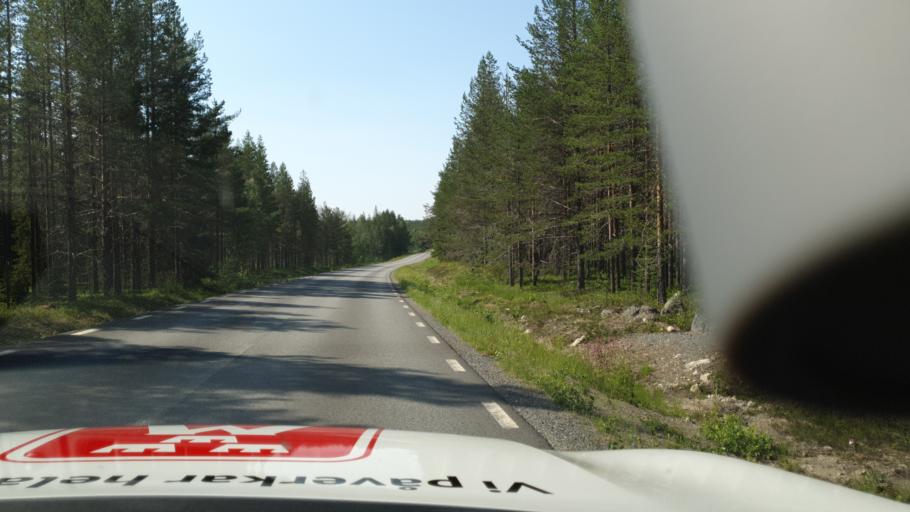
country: SE
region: Vaesterbotten
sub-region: Skelleftea Kommun
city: Langsele
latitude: 64.9900
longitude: 20.0857
